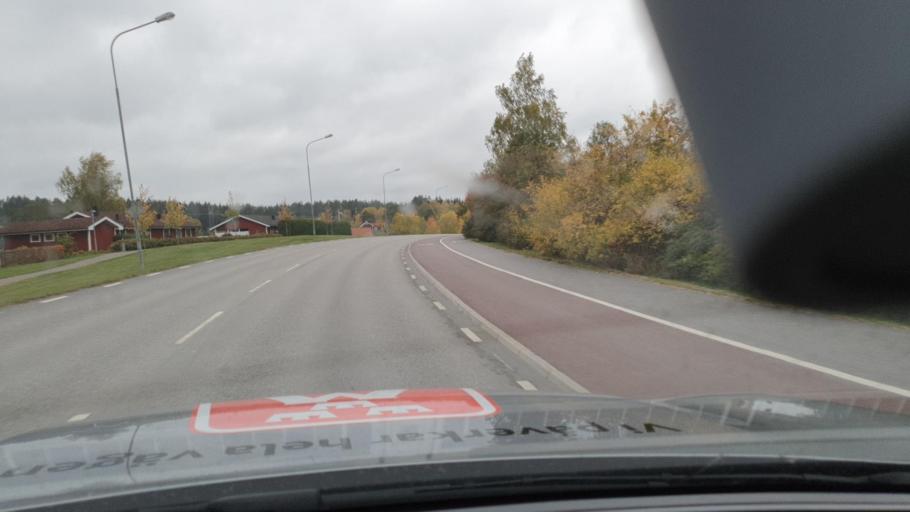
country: SE
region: OEstergoetland
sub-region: Soderkopings Kommun
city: Soederkoeping
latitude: 58.4714
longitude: 16.3139
